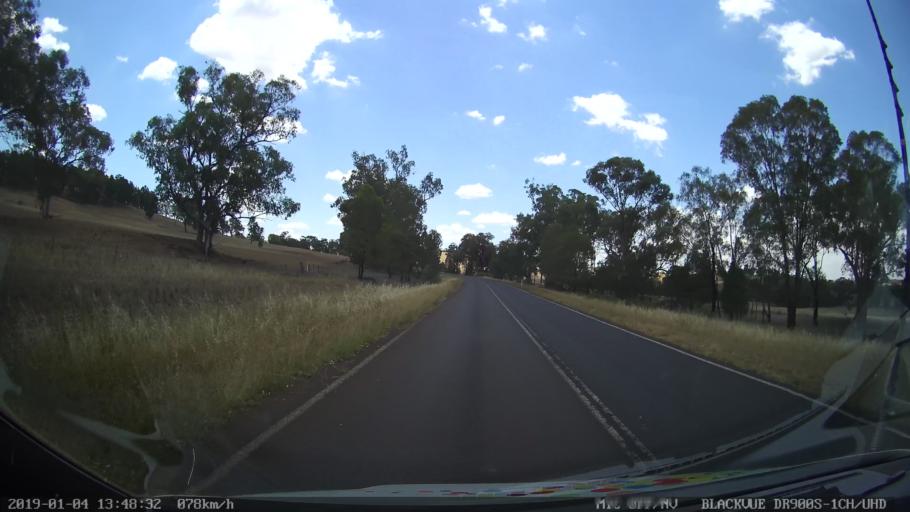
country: AU
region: New South Wales
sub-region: Dubbo Municipality
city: Dubbo
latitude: -32.4415
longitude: 148.5844
